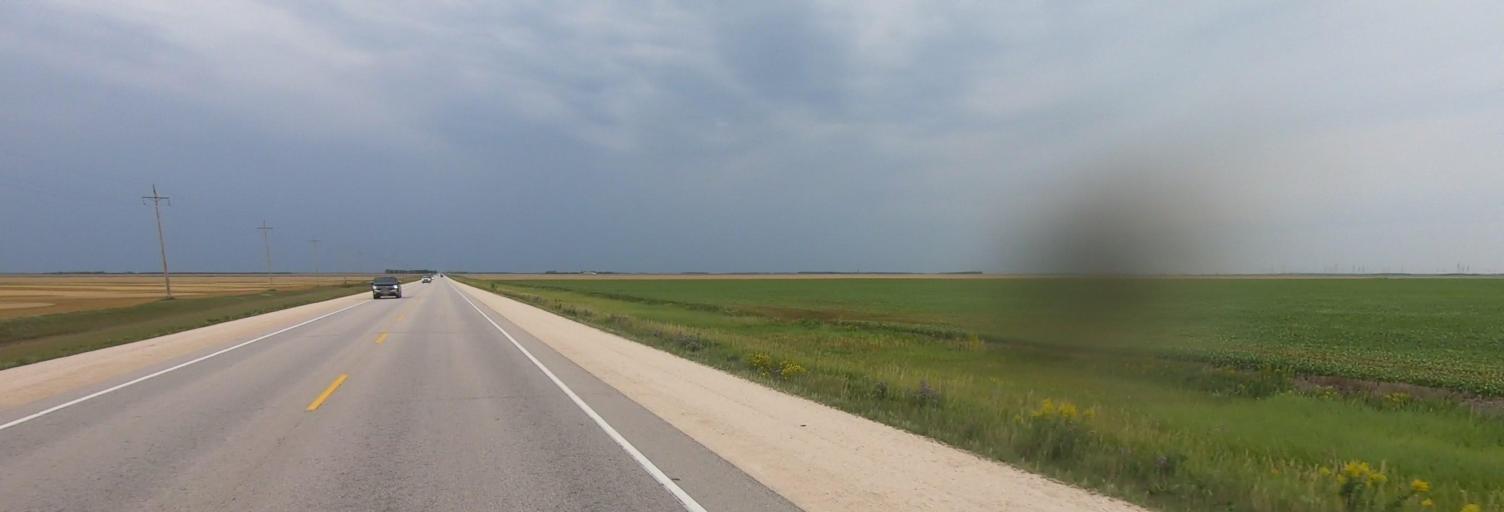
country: CA
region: Manitoba
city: Headingley
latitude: 49.7686
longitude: -97.3958
